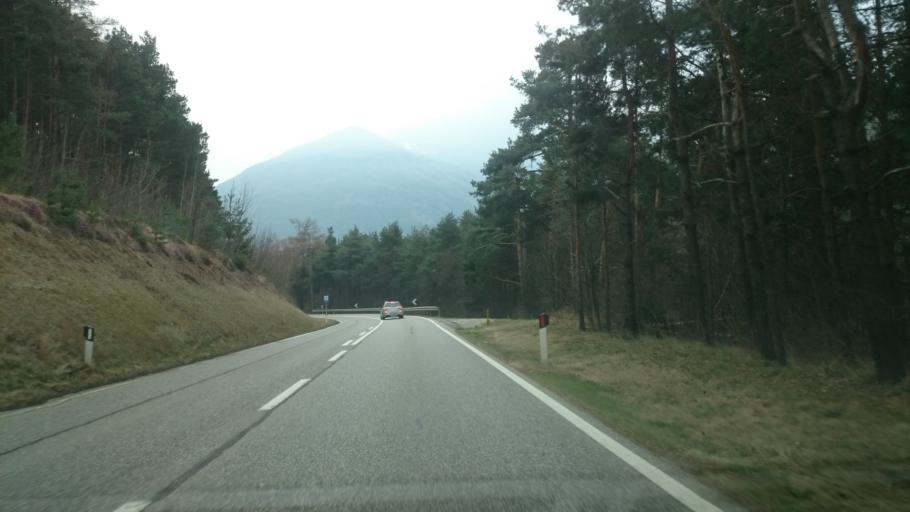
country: IT
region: Trentino-Alto Adige
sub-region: Bolzano
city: Naz-Sciaves - Natz-Schabs
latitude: 46.7574
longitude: 11.6522
